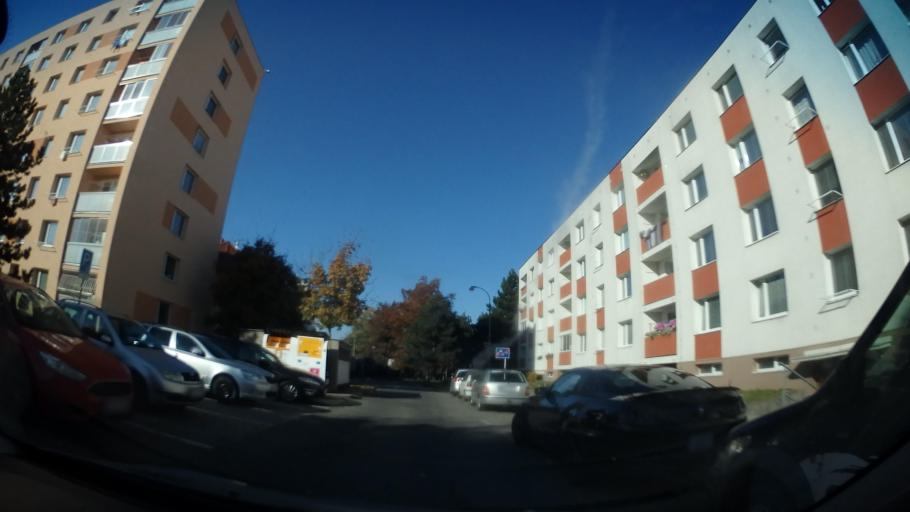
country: CZ
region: Pardubicky
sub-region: Okres Chrudim
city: Chrudim
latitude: 49.9497
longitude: 15.7915
